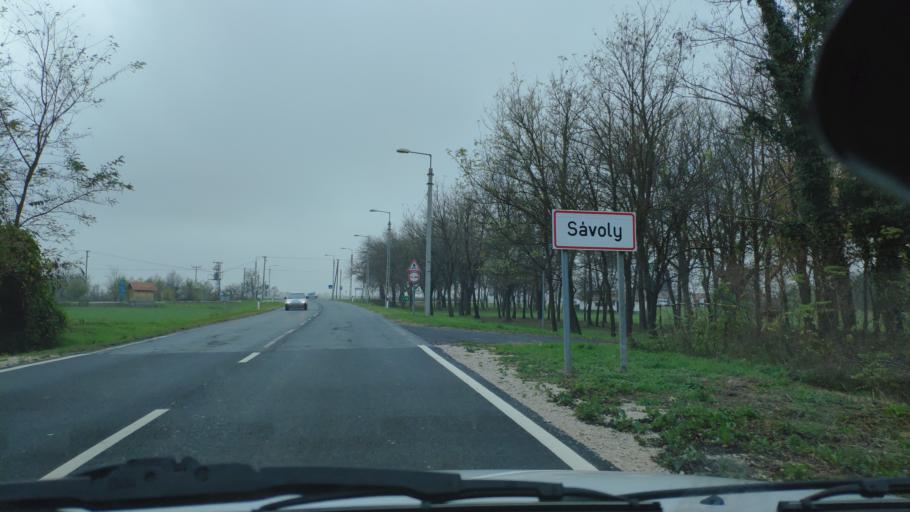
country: HU
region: Zala
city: Zalakomar
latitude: 46.6018
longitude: 17.2655
